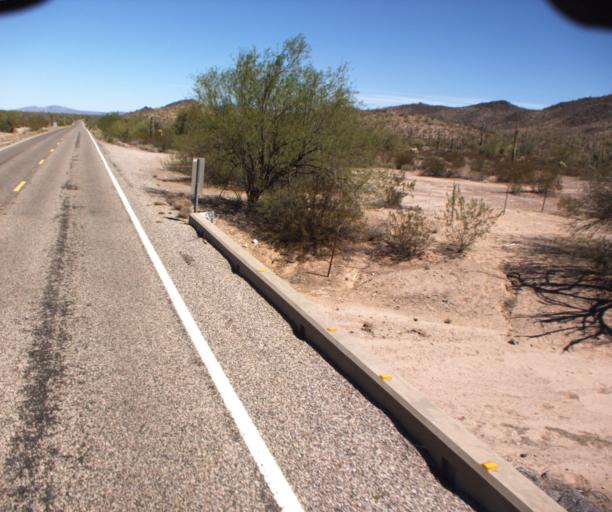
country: US
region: Arizona
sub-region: Pima County
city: Ajo
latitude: 32.2081
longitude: -112.7585
